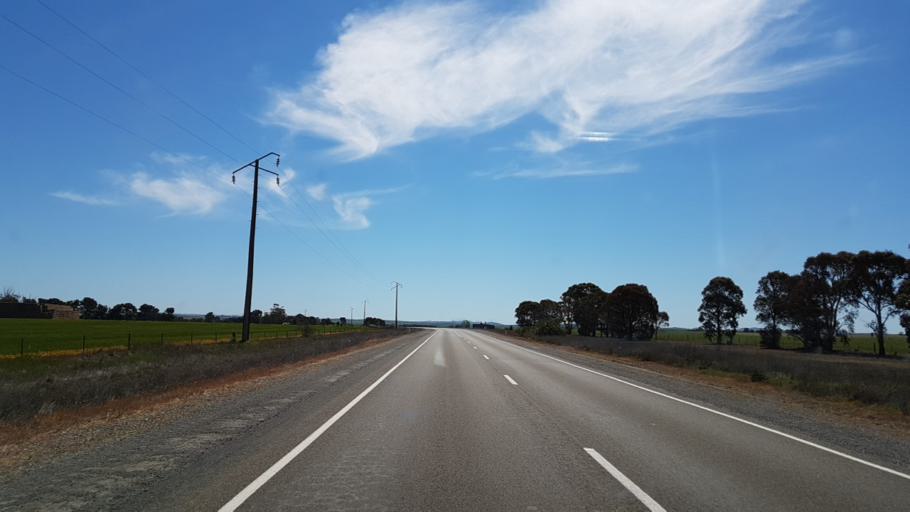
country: AU
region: South Australia
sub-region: Clare and Gilbert Valleys
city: Clare
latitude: -33.7707
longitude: 138.8440
